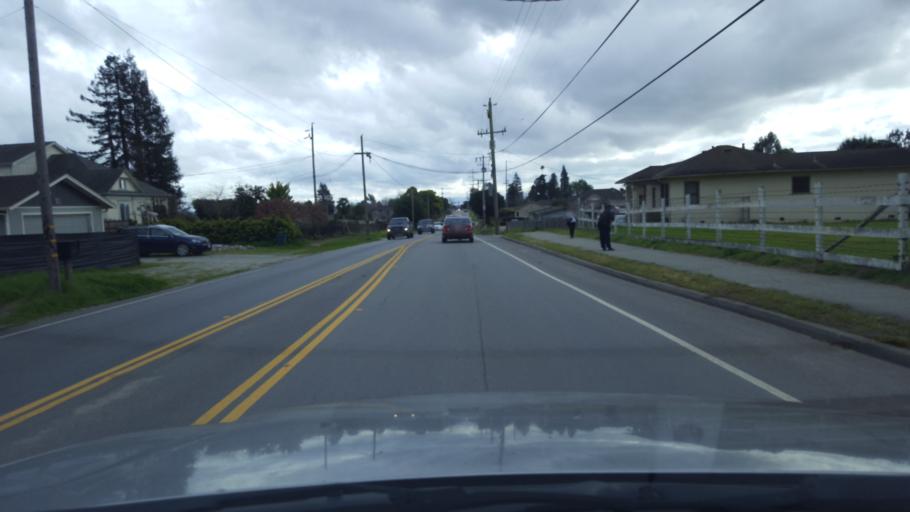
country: US
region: California
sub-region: Santa Cruz County
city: Amesti
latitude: 36.9555
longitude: -121.7650
